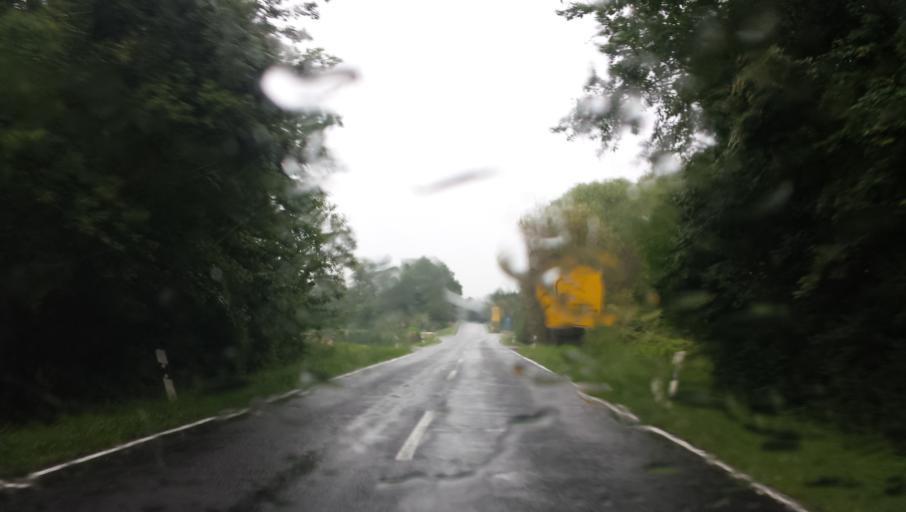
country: DE
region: Rheinland-Pfalz
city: Bobenheim-Roxheim
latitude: 49.6072
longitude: 8.3756
